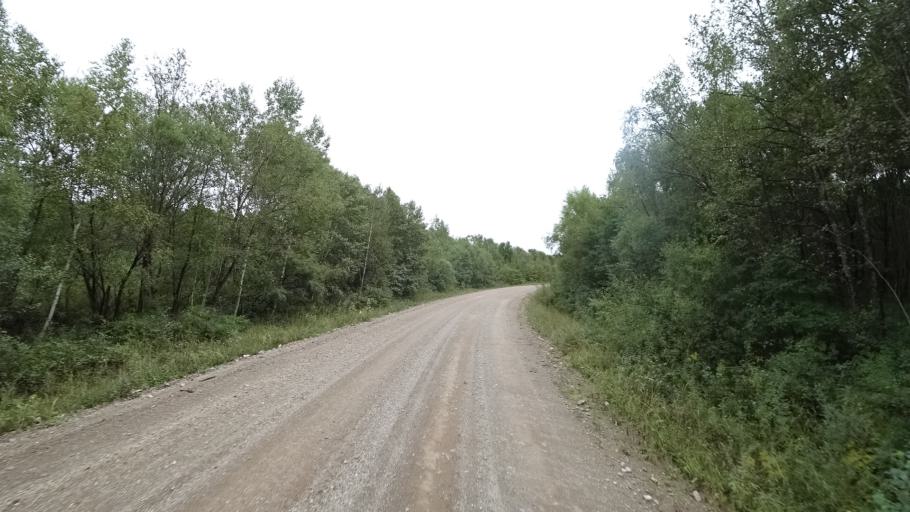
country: RU
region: Primorskiy
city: Ivanovka
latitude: 44.0272
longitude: 132.5159
